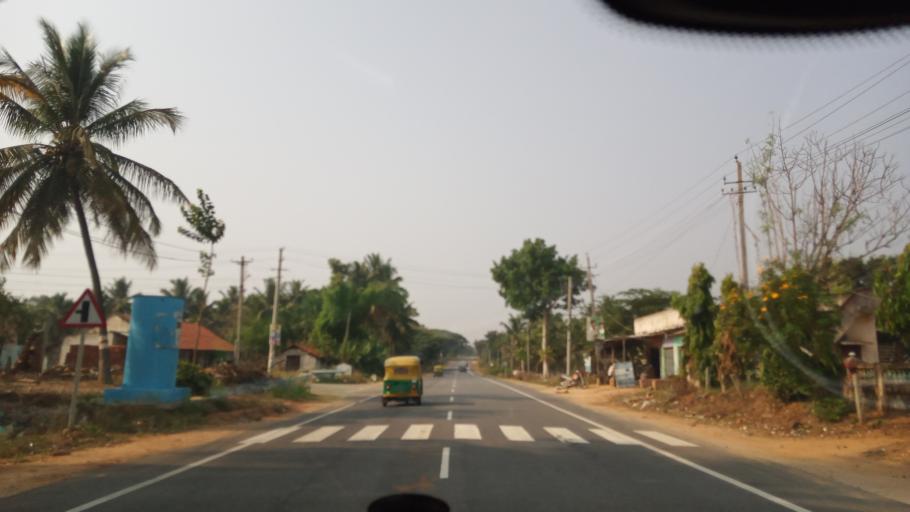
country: IN
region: Karnataka
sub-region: Mandya
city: Belluru
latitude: 12.9303
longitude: 76.7496
